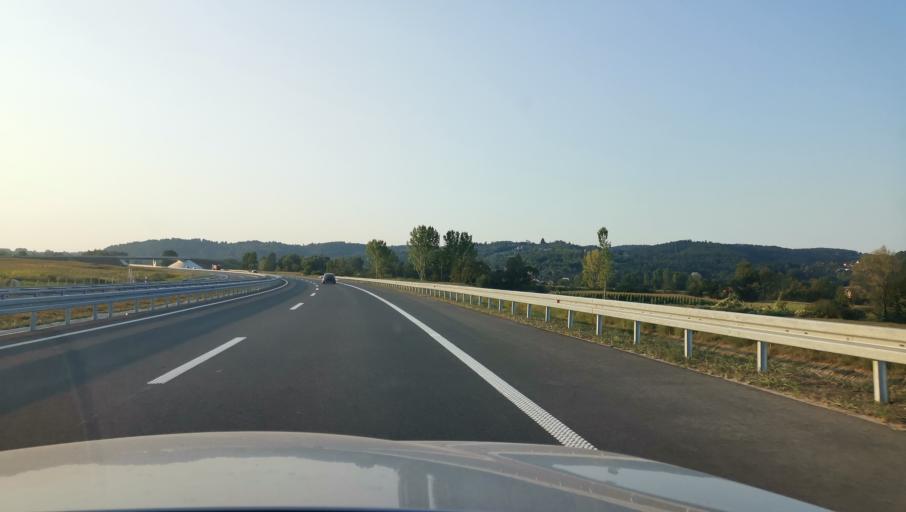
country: RS
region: Central Serbia
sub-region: Kolubarski Okrug
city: Lajkovac
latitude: 44.3271
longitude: 20.2127
